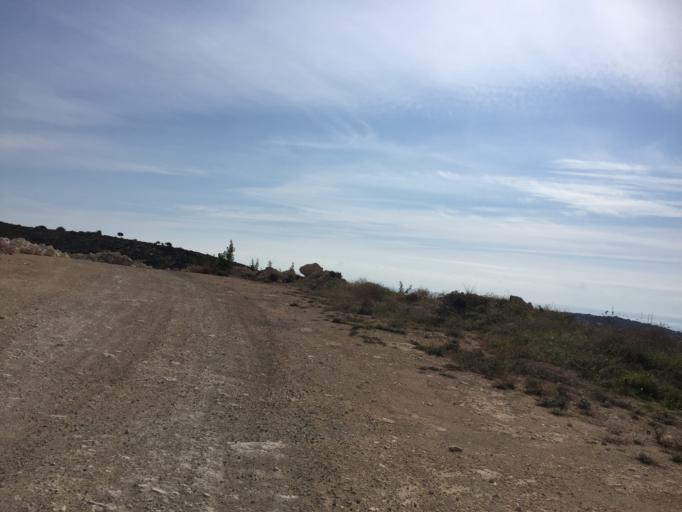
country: CY
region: Larnaka
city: Agios Tychon
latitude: 34.7426
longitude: 33.1194
